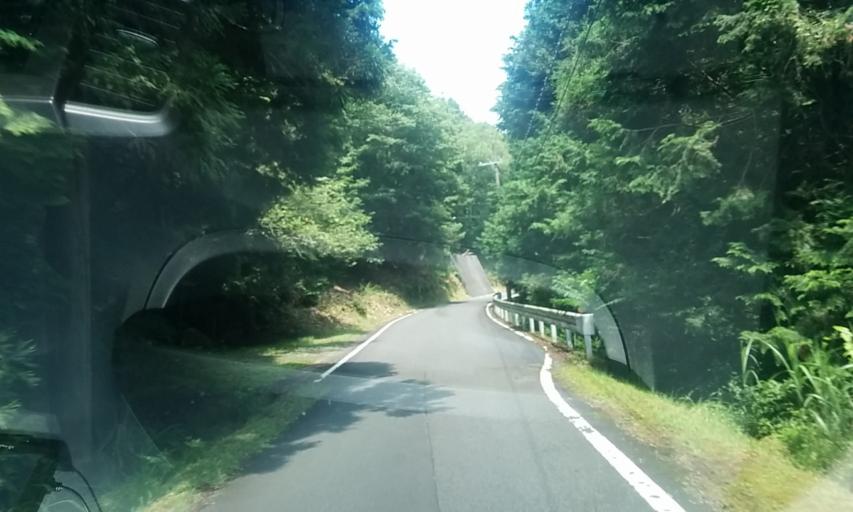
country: JP
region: Hyogo
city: Sasayama
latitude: 35.1849
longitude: 135.2162
